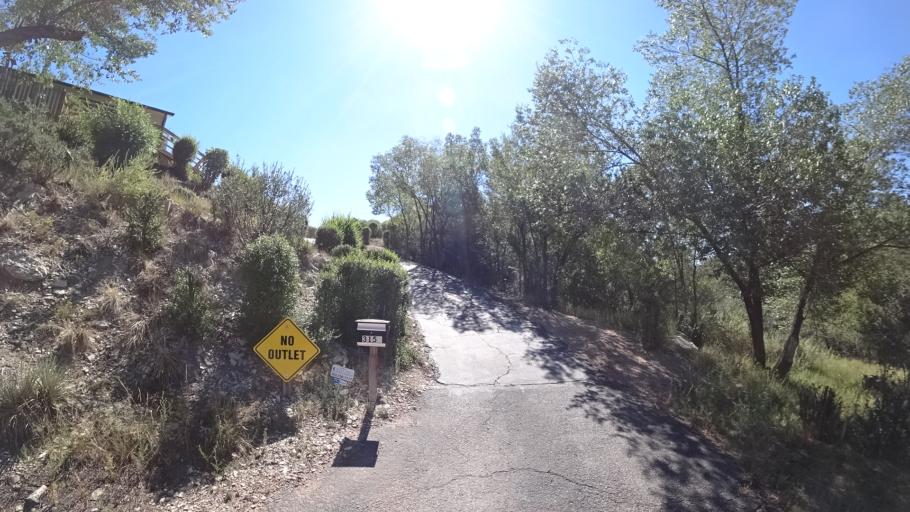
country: US
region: Colorado
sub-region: El Paso County
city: Manitou Springs
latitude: 38.8558
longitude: -104.8728
